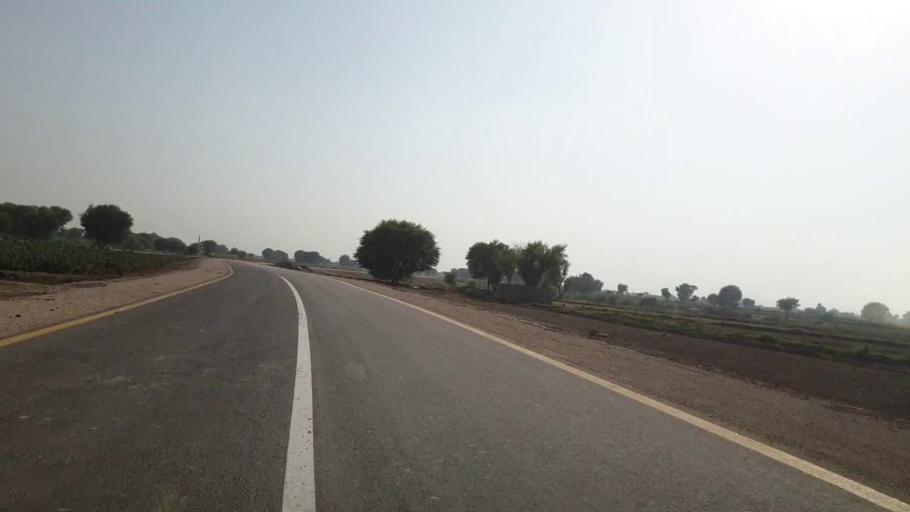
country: PK
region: Sindh
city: Bhan
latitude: 26.5086
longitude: 67.7842
